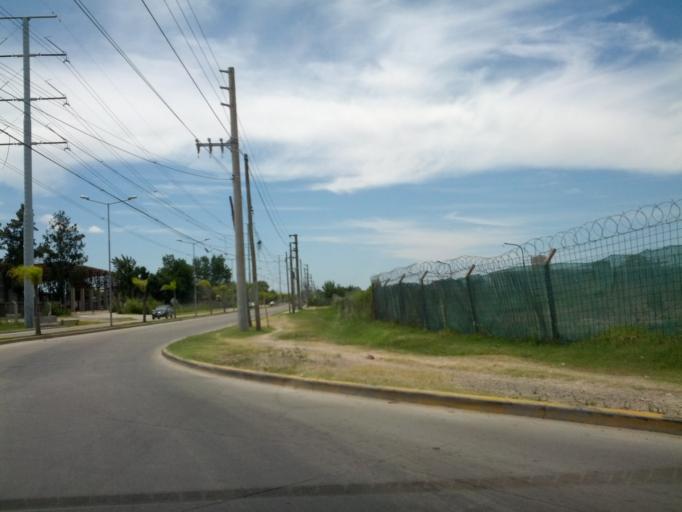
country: AR
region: Buenos Aires
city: Santa Catalina - Dique Lujan
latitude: -34.4029
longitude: -58.6795
